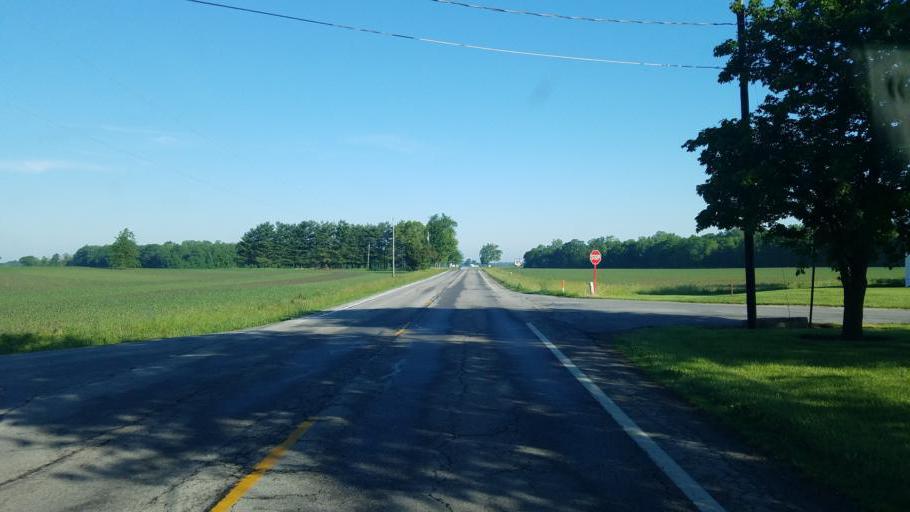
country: US
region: Ohio
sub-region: Morrow County
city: Mount Gilead
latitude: 40.5603
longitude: -82.8715
